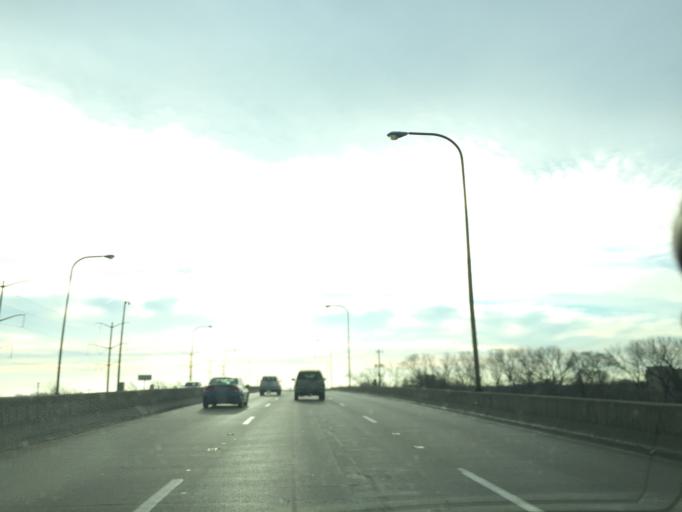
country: US
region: Illinois
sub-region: Cook County
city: Chicago
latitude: 41.7572
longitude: -87.5962
